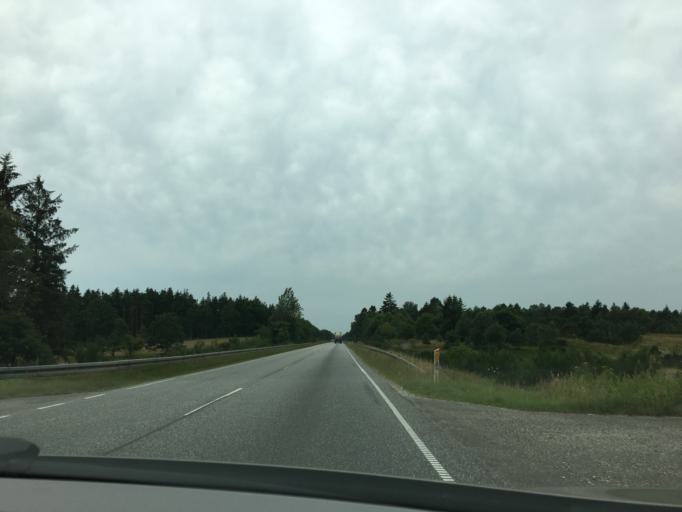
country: DK
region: Central Jutland
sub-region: Herning Kommune
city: Sunds
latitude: 56.3753
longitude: 8.9851
